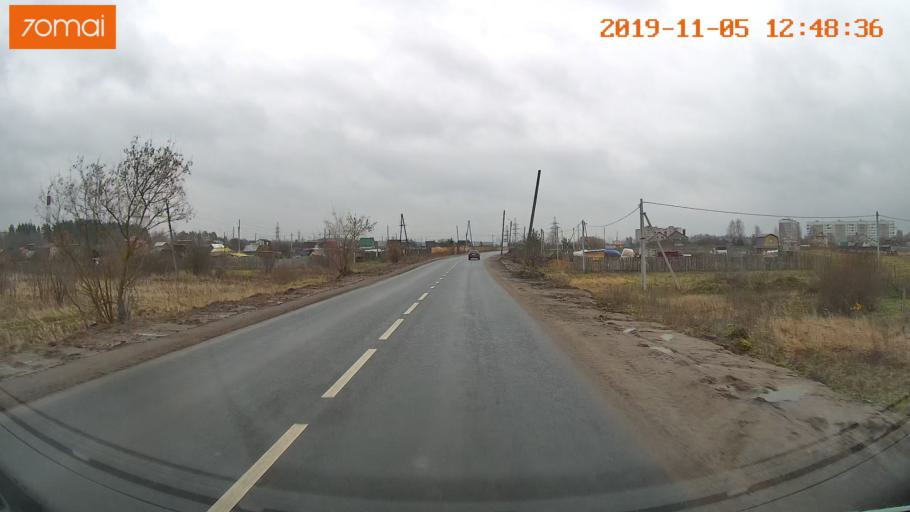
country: RU
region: Ivanovo
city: Kokhma
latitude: 56.9599
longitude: 41.0988
